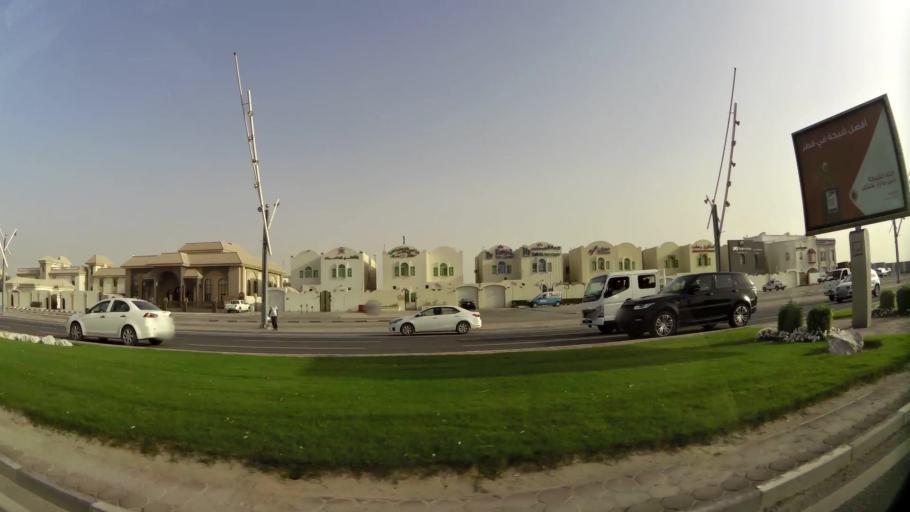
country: QA
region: Baladiyat ar Rayyan
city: Ar Rayyan
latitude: 25.2541
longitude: 51.4360
